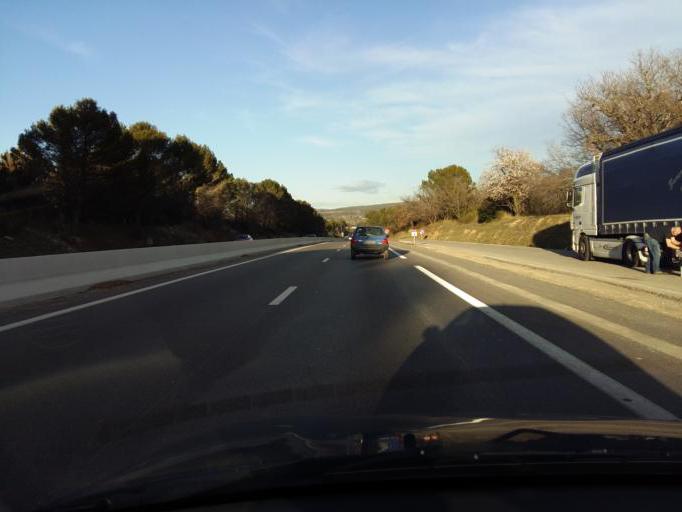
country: FR
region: Provence-Alpes-Cote d'Azur
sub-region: Departement des Bouches-du-Rhone
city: Aix-en-Provence
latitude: 43.5548
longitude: 5.4392
